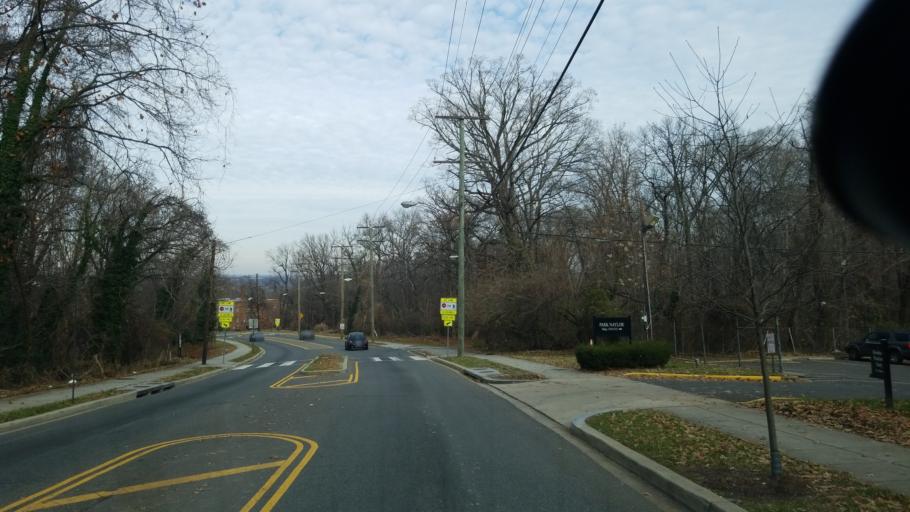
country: US
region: Maryland
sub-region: Prince George's County
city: Silver Hill
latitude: 38.8659
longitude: -76.9703
